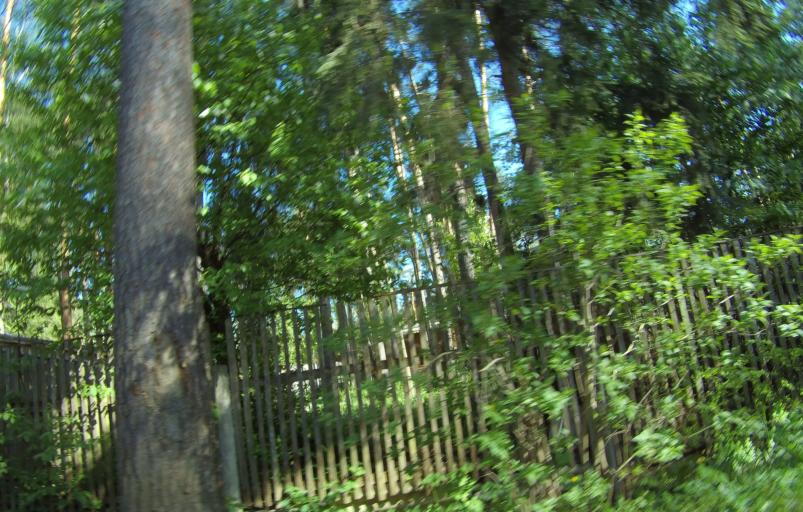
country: RU
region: Moskovskaya
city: Kratovo
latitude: 55.5870
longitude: 38.1798
